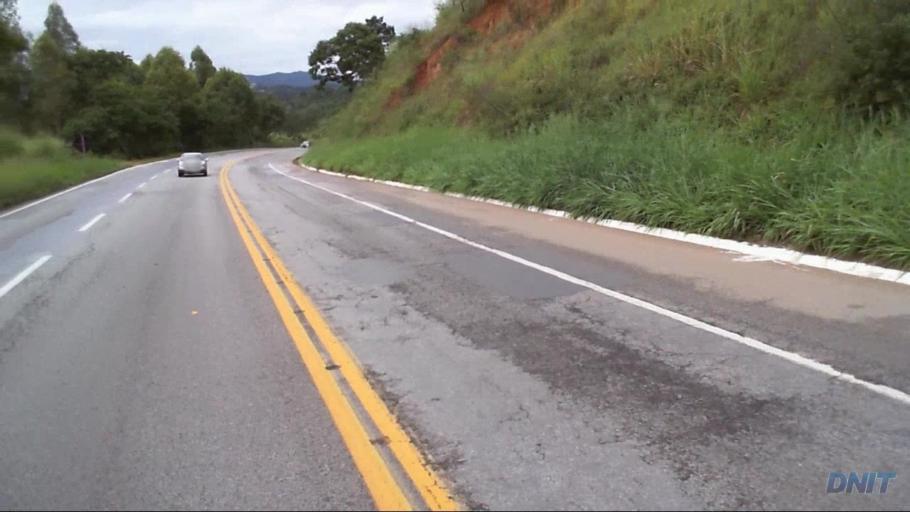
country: BR
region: Minas Gerais
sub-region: Barao De Cocais
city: Barao de Cocais
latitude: -19.8351
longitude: -43.3692
